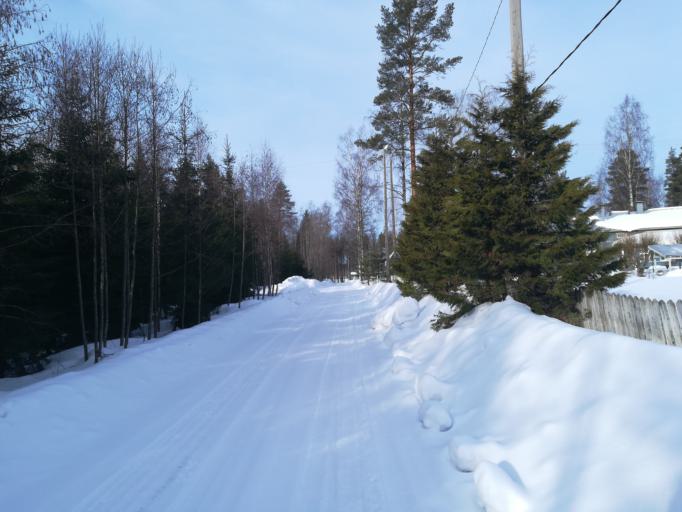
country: FI
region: Southern Savonia
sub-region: Savonlinna
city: Savonlinna
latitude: 61.8280
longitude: 29.0264
